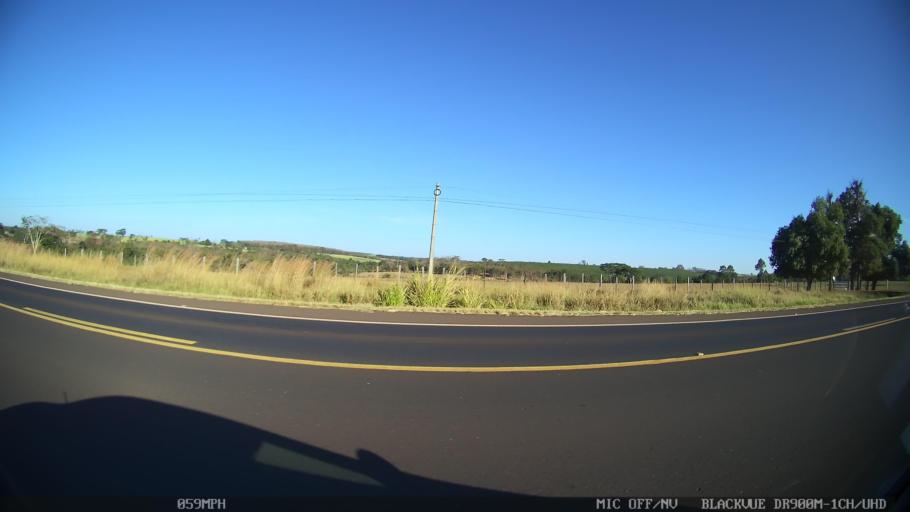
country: BR
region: Sao Paulo
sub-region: Olimpia
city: Olimpia
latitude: -20.7107
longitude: -48.9762
